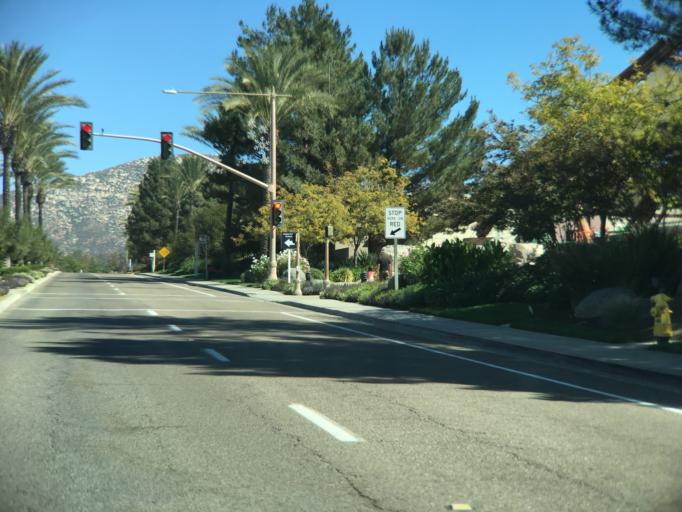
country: US
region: California
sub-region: San Diego County
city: Alpine
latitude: 32.8412
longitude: -116.7060
